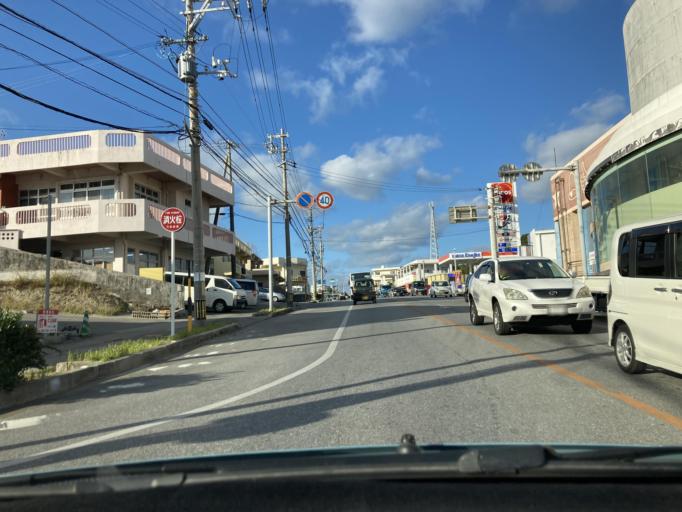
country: JP
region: Okinawa
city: Gushikawa
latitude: 26.3479
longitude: 127.8705
